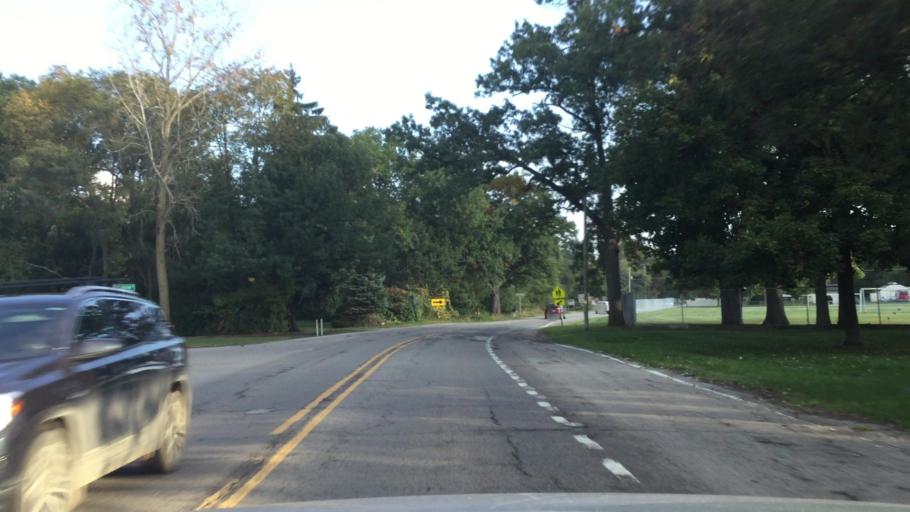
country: US
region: Michigan
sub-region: Oakland County
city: Waterford
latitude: 42.6360
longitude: -83.4666
